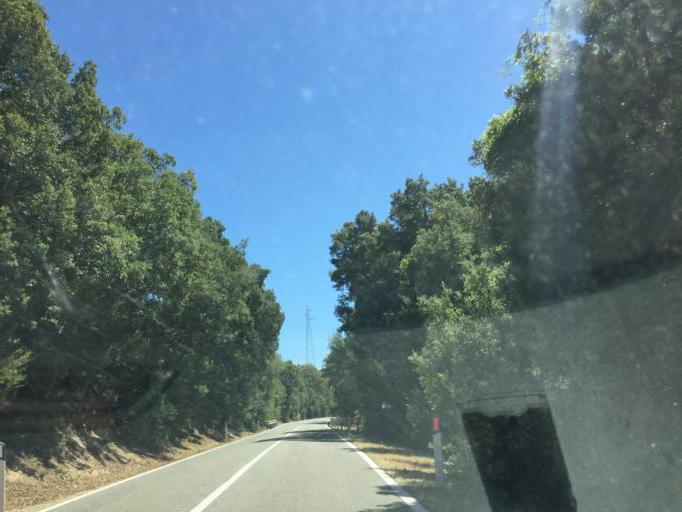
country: IT
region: Sardinia
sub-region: Provincia di Olbia-Tempio
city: Telti
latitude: 40.8976
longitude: 9.2804
